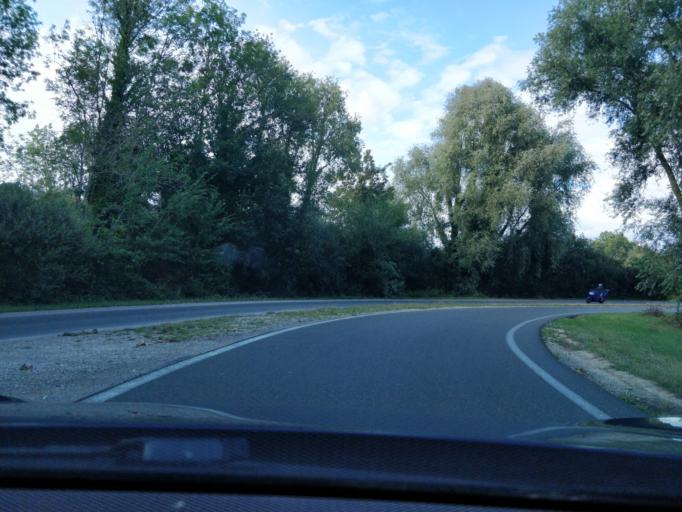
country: FR
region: Ile-de-France
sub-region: Departement de l'Essonne
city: Etampes
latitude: 48.4282
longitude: 2.1537
